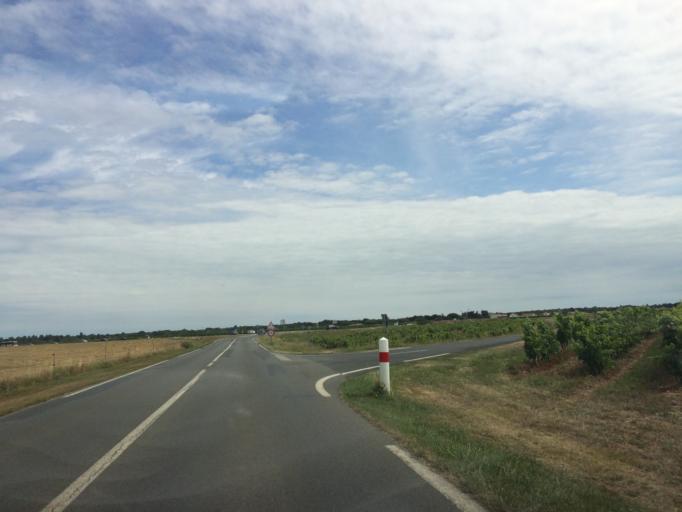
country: FR
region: Poitou-Charentes
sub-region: Departement de la Charente-Maritime
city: Saint-Martin-de-Re
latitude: 46.1996
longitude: -1.3731
